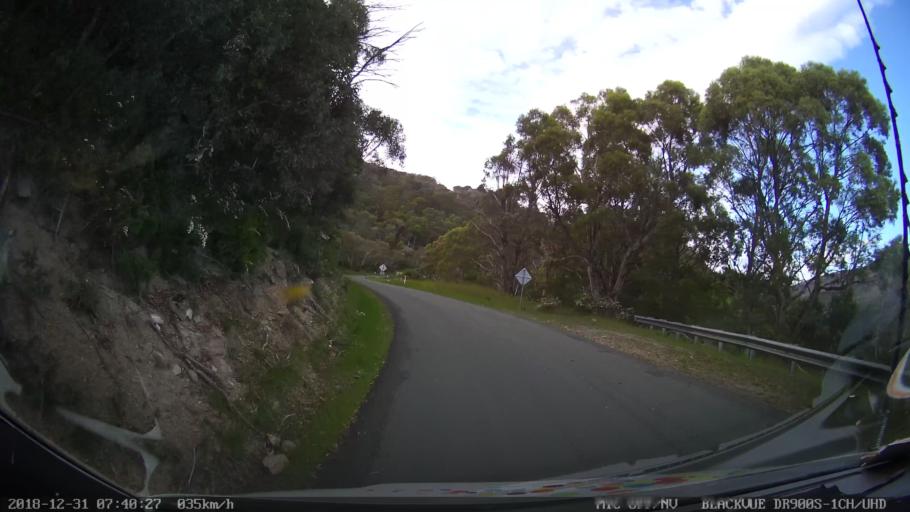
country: AU
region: New South Wales
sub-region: Snowy River
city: Jindabyne
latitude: -36.3506
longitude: 148.4164
